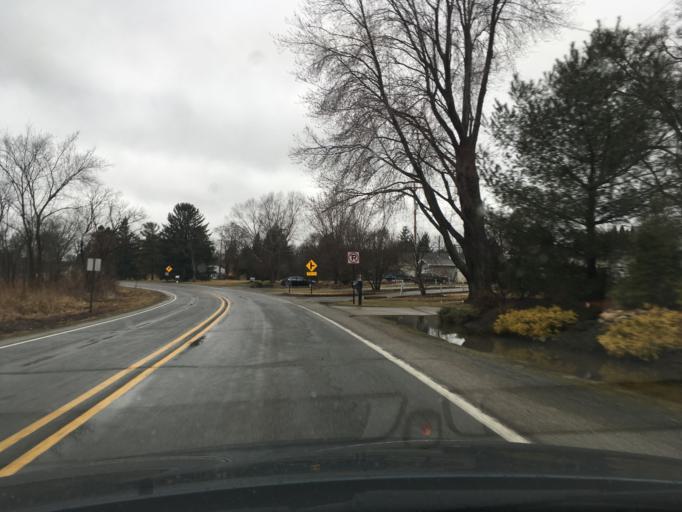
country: US
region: Michigan
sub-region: Washtenaw County
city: Chelsea
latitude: 42.3116
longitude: -84.1016
